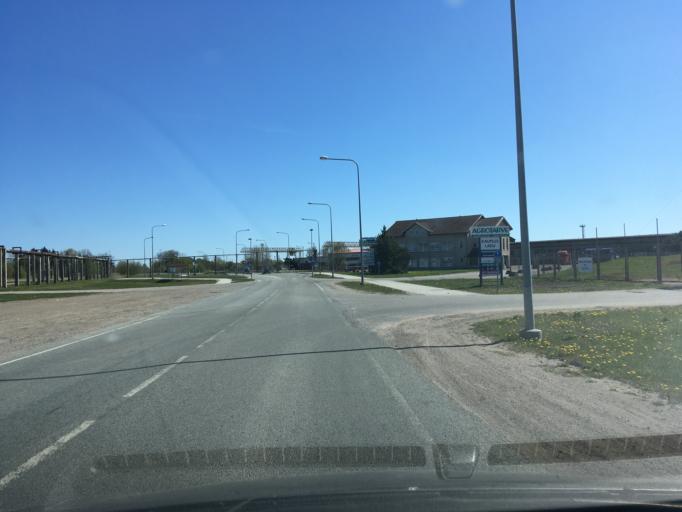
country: EE
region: Harju
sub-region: Joelaehtme vald
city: Loo
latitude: 59.4532
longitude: 24.9643
